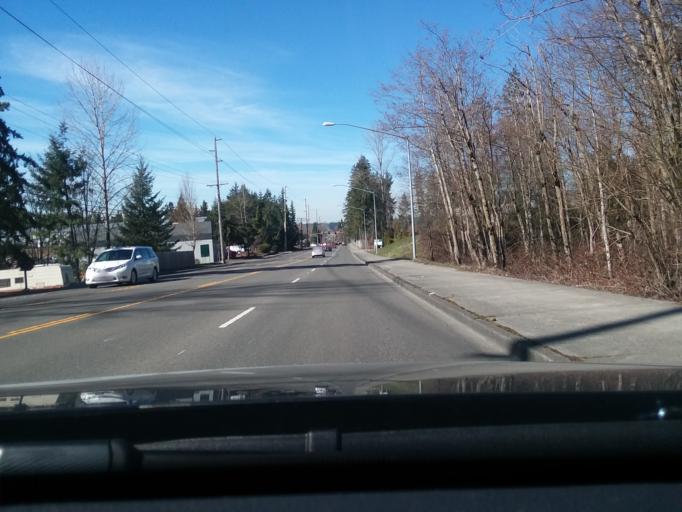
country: US
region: Washington
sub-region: Pierce County
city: South Hill
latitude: 47.1547
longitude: -122.2776
